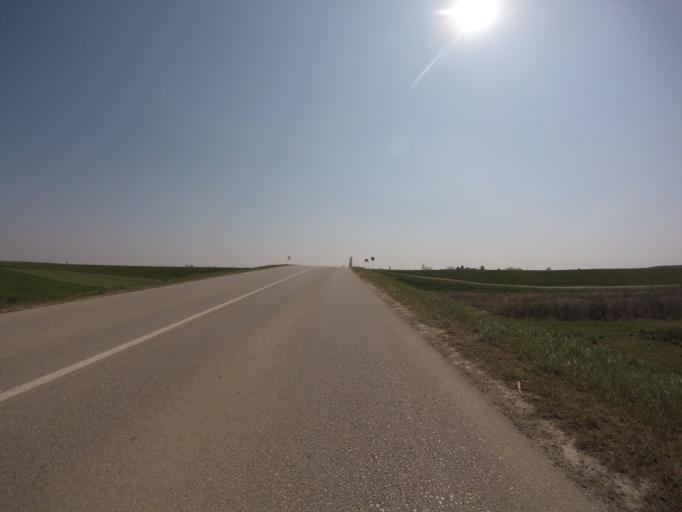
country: HR
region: Zagrebacka
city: Lukavec
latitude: 45.7109
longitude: 15.9956
